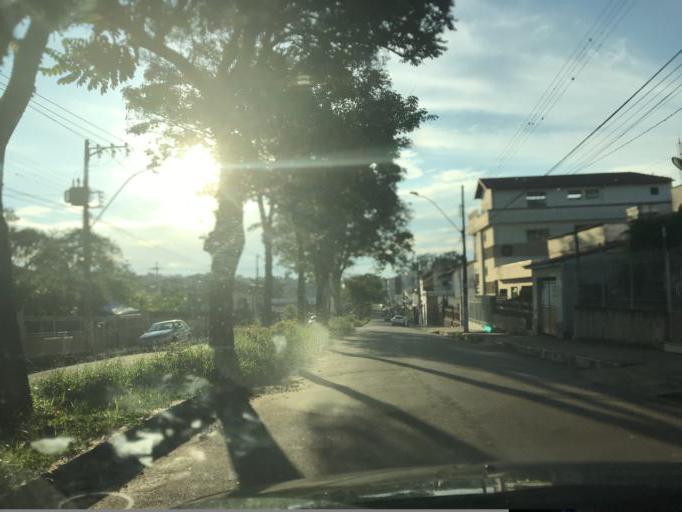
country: BR
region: Minas Gerais
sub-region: Tres Coracoes
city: Tres Coracoes
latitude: -21.7035
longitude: -45.2505
